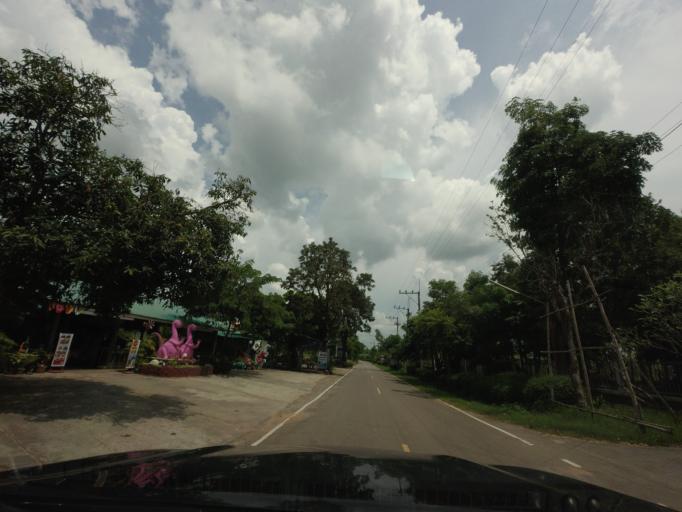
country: TH
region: Khon Kaen
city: Wiang Kao
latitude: 16.6792
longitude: 102.2677
